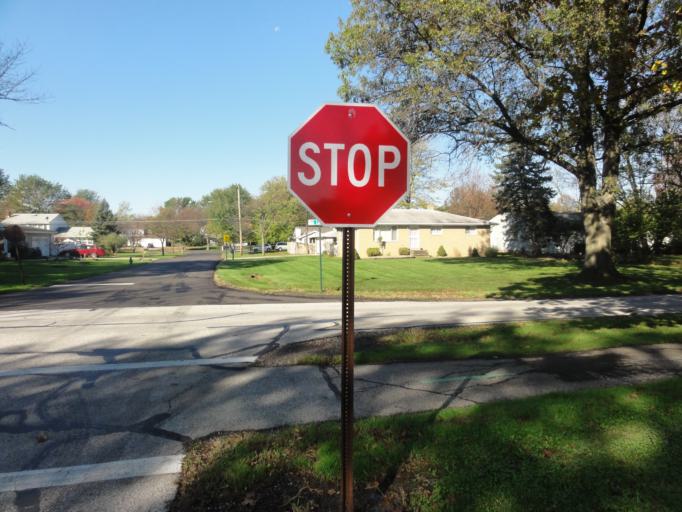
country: US
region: Ohio
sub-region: Cuyahoga County
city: Middleburg Heights
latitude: 41.3453
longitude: -81.8294
